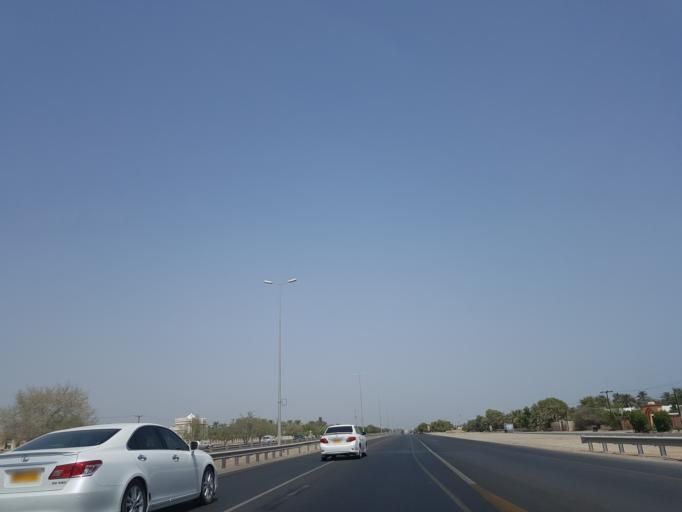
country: OM
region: Al Batinah
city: Saham
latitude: 24.0787
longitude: 56.9416
